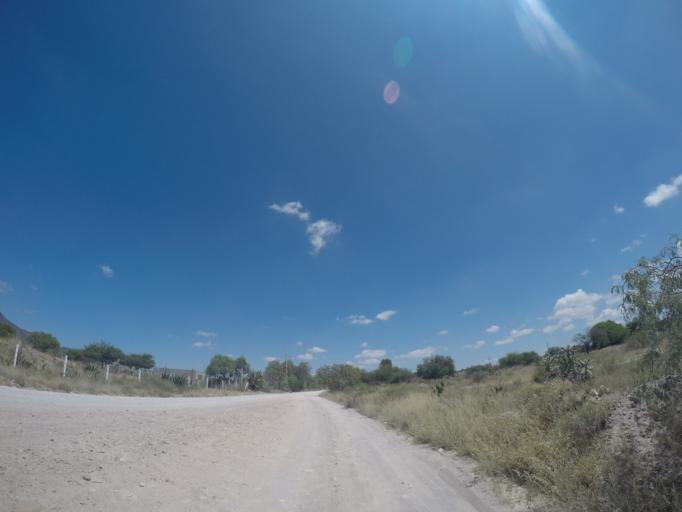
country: MX
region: San Luis Potosi
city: La Pila
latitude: 21.9952
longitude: -100.8988
